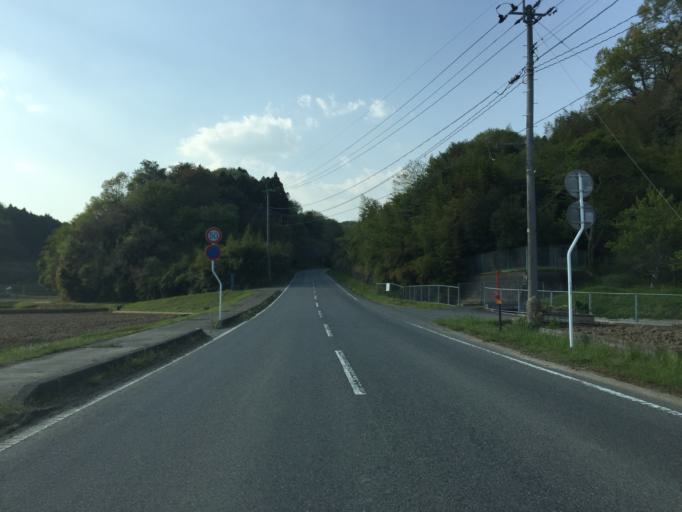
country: JP
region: Fukushima
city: Iwaki
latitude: 36.9686
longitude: 140.8395
